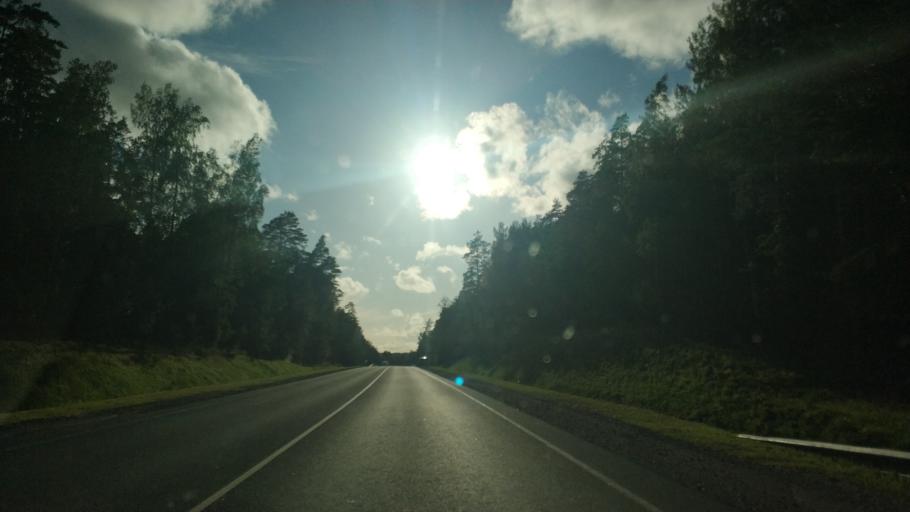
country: RU
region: Leningrad
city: Sapernoye
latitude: 60.7158
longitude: 30.0061
